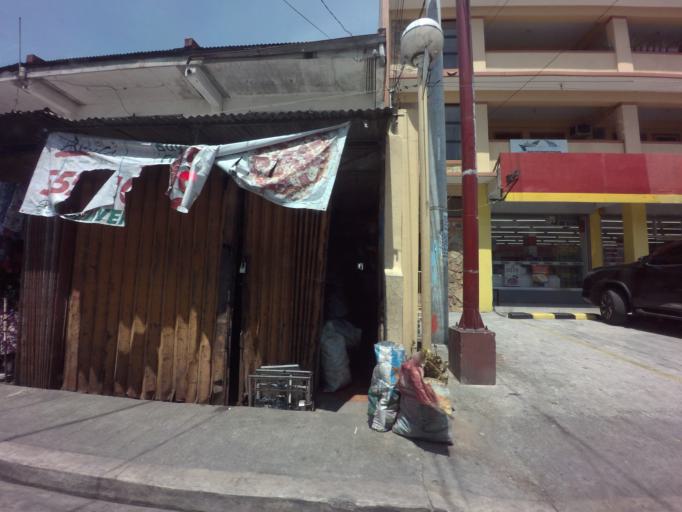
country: PH
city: Sambayanihan People's Village
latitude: 14.4300
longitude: 121.0131
